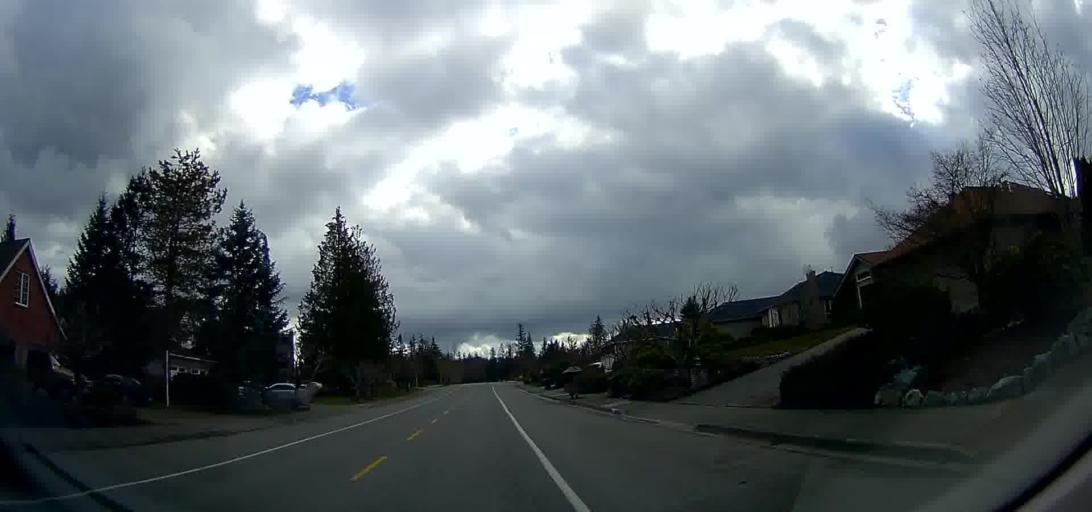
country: US
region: Washington
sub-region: Skagit County
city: Mount Vernon
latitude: 48.4174
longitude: -122.2869
